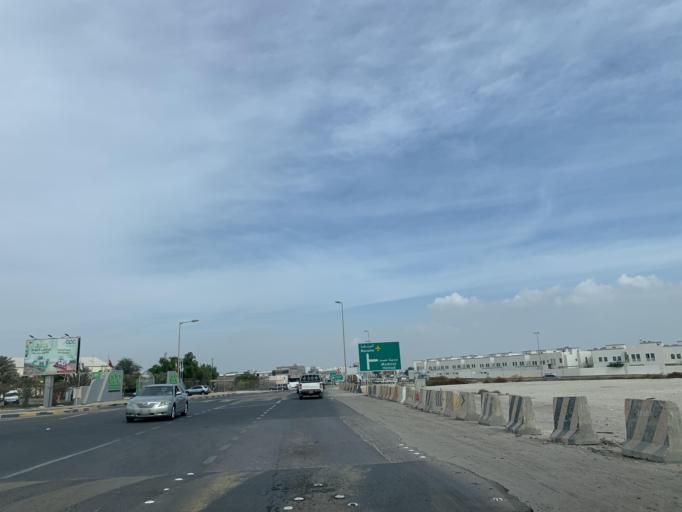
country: BH
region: Central Governorate
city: Madinat Hamad
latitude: 26.1322
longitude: 50.4803
